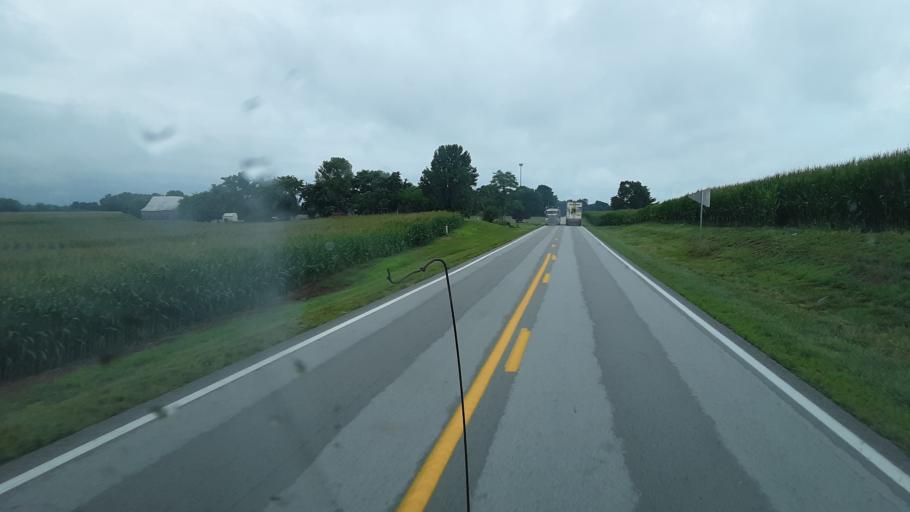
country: US
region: Kentucky
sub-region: Todd County
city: Elkton
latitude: 36.7471
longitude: -87.0491
